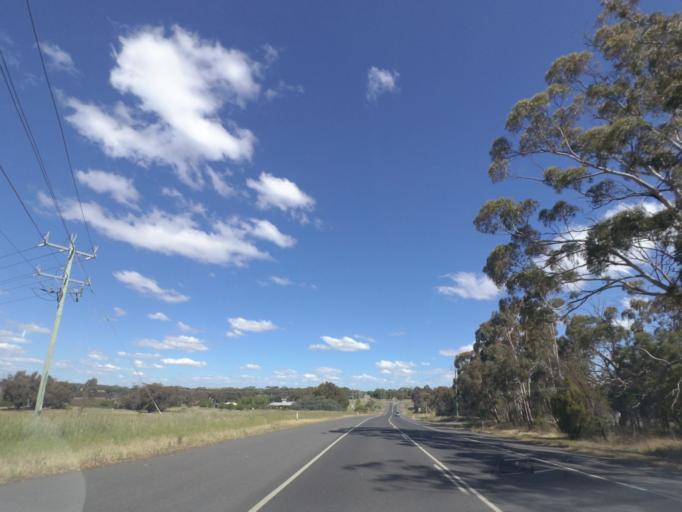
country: AU
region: Victoria
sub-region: Hume
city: Sunbury
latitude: -37.4530
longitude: 144.5767
